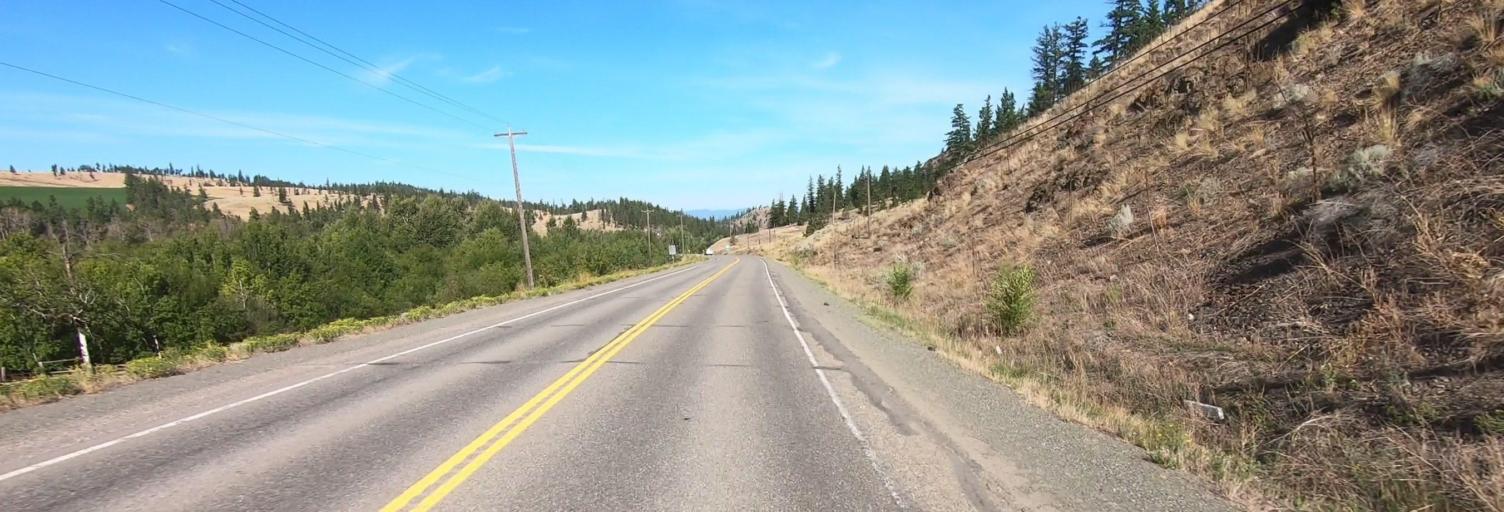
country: CA
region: British Columbia
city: Kamloops
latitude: 50.6639
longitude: -120.5564
